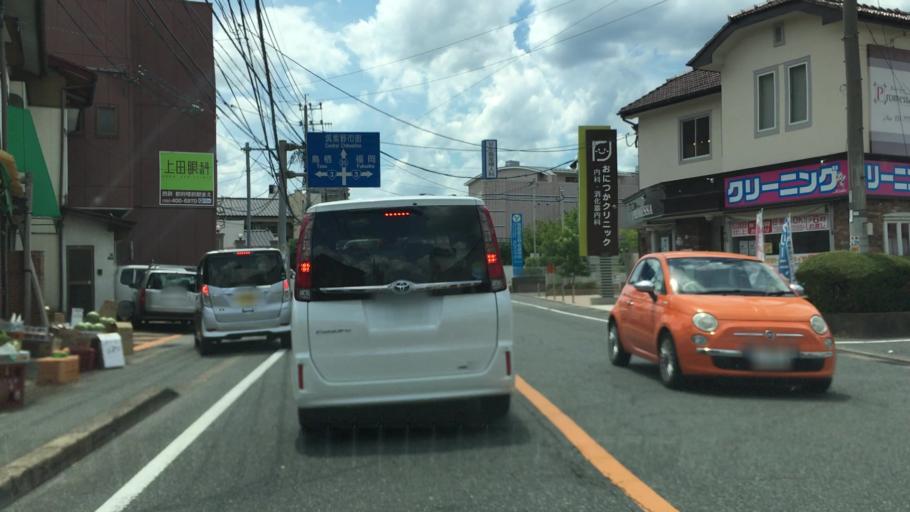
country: JP
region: Fukuoka
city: Dazaifu
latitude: 33.5095
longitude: 130.5244
